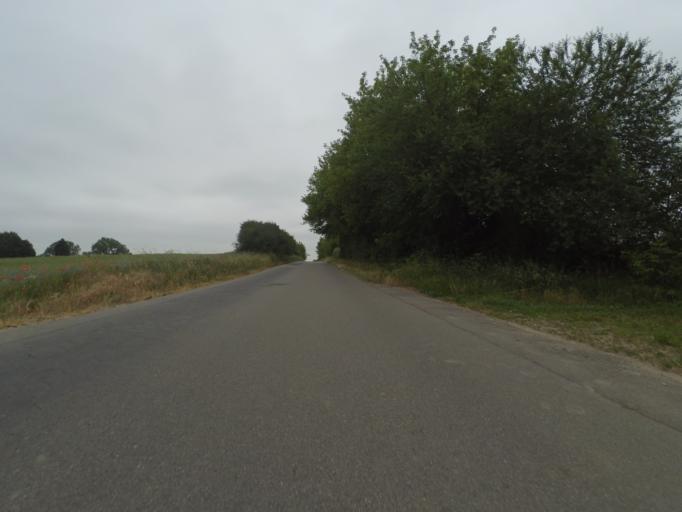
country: DE
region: Mecklenburg-Vorpommern
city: Goldberg
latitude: 53.5624
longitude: 12.1017
